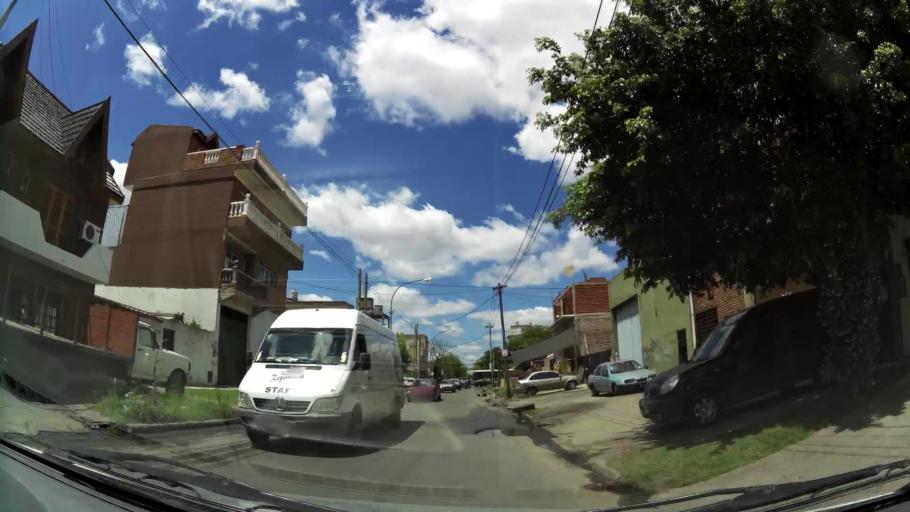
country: AR
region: Buenos Aires
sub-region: Partido de Lanus
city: Lanus
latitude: -34.7016
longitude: -58.4279
